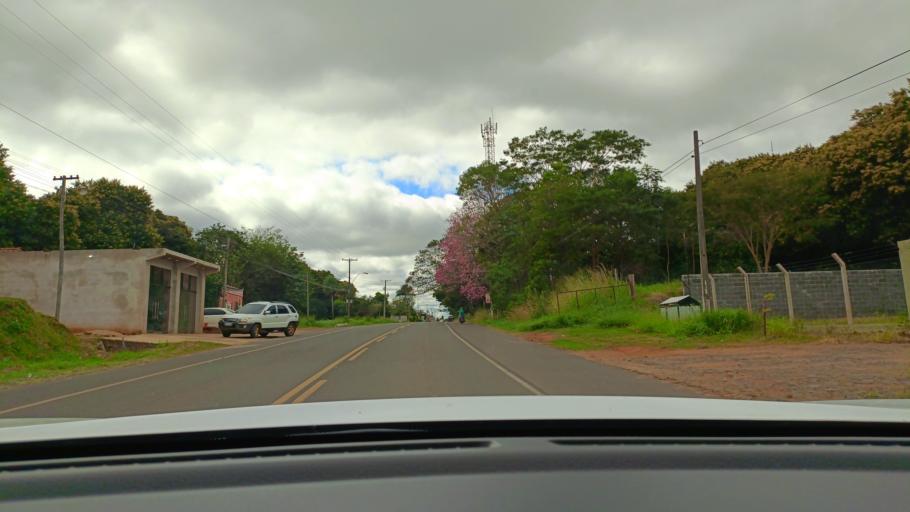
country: PY
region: San Pedro
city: Union
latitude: -24.6799
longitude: -56.4646
